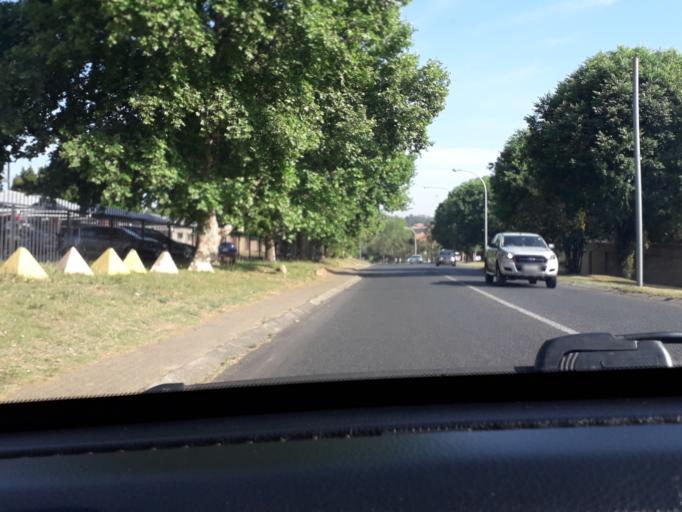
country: ZA
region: Gauteng
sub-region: City of Johannesburg Metropolitan Municipality
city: Modderfontein
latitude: -26.1588
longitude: 28.1296
